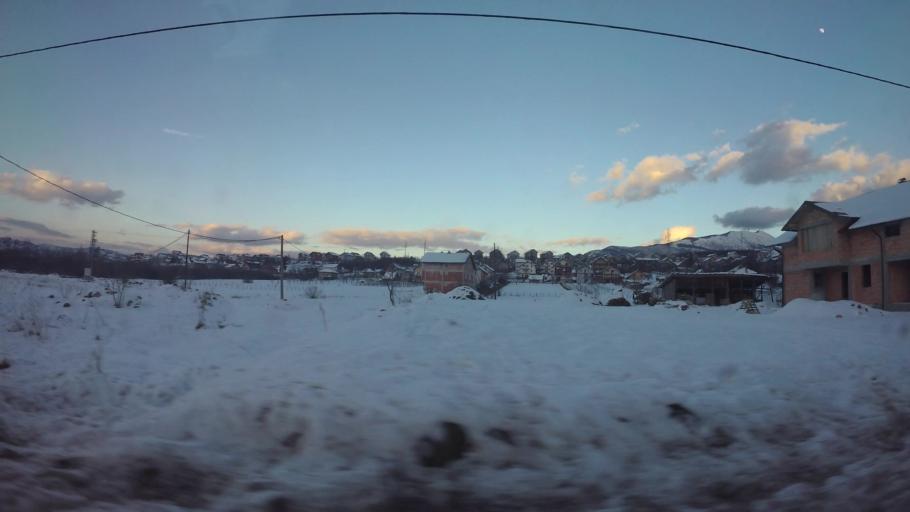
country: BA
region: Federation of Bosnia and Herzegovina
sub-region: Kanton Sarajevo
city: Sarajevo
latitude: 43.8114
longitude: 18.3714
